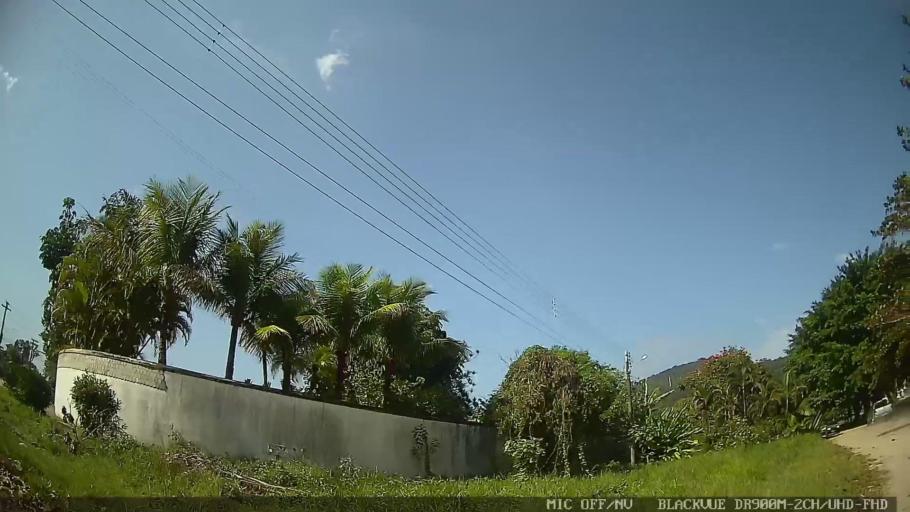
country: BR
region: Sao Paulo
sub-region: Guaruja
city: Guaruja
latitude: -23.9772
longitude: -46.2005
